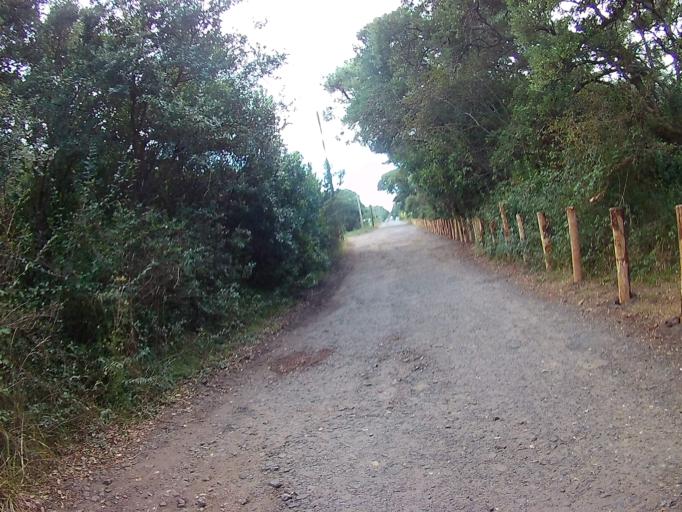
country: FR
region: Aquitaine
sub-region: Departement des Landes
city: Labenne
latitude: 43.6045
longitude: -1.4656
